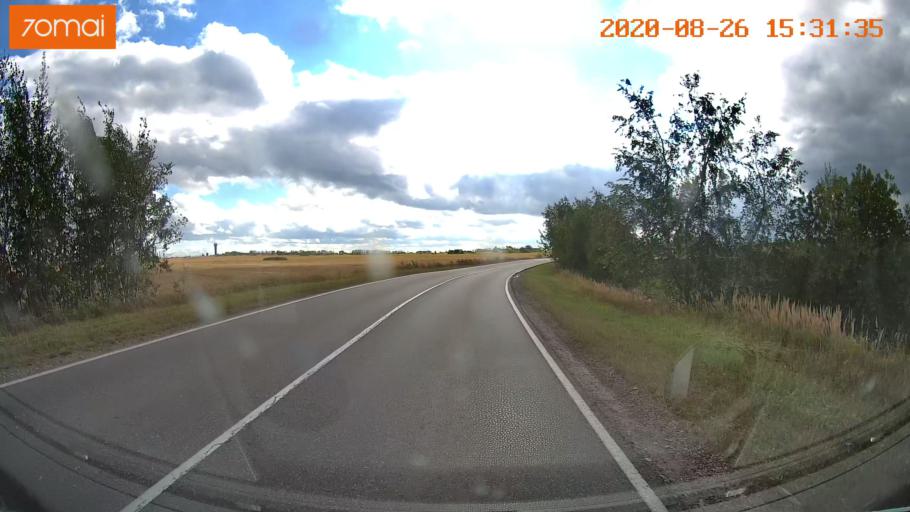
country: RU
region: Tula
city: Severo-Zadonsk
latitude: 54.0779
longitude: 38.3845
